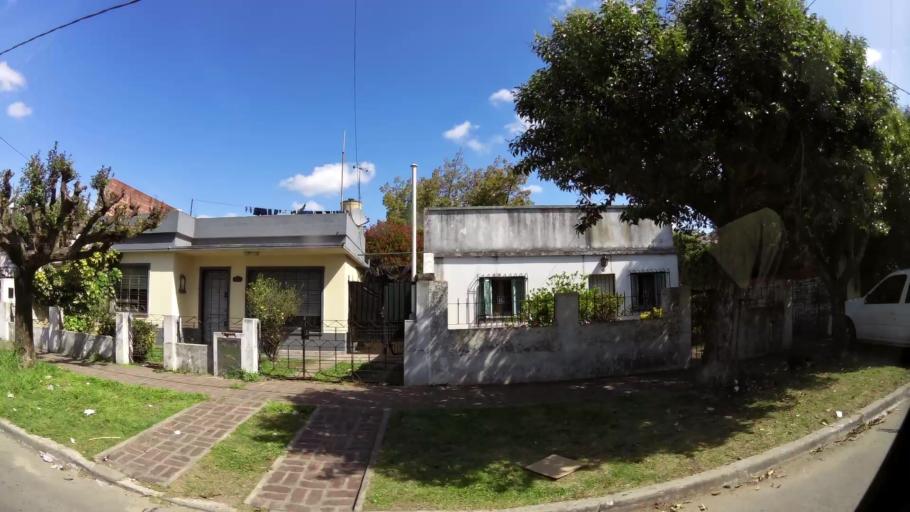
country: AR
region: Buenos Aires
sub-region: Partido de Quilmes
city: Quilmes
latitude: -34.8052
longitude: -58.2639
